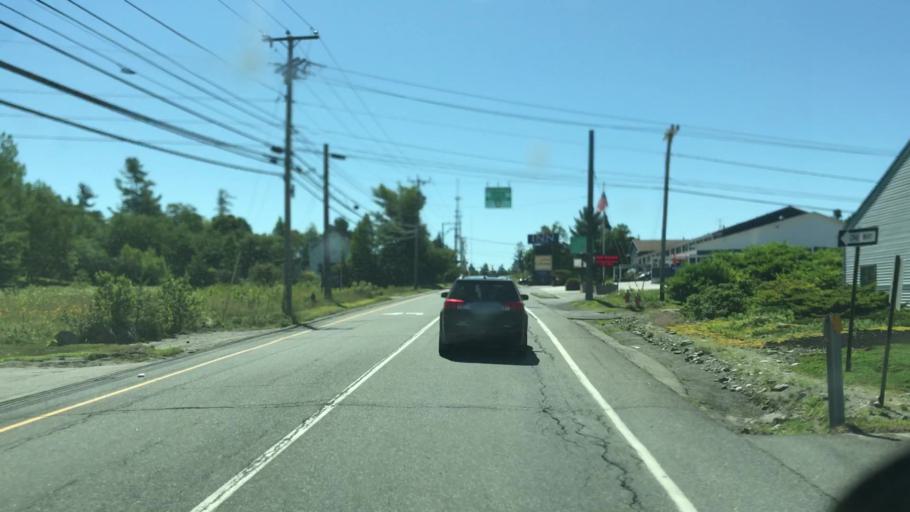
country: US
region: Maine
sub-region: Hancock County
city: Ellsworth
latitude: 44.5266
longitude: -68.4011
